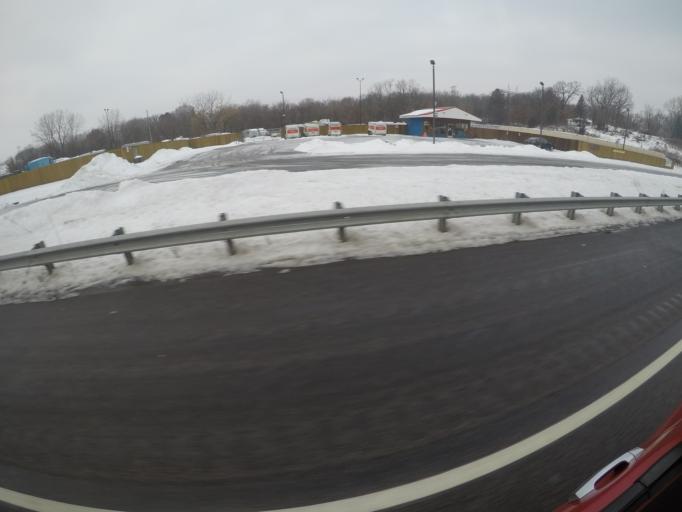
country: US
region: Minnesota
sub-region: Dakota County
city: Inver Grove Heights
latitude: 44.8030
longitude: -93.0397
